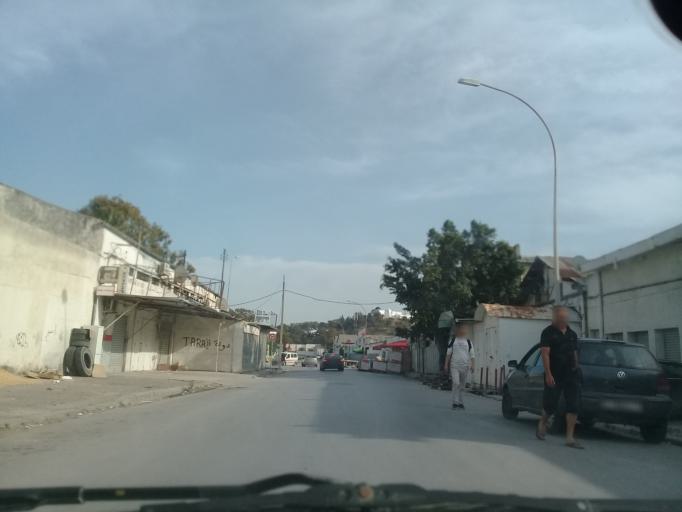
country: TN
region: Tunis
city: Tunis
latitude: 36.7936
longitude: 10.1873
